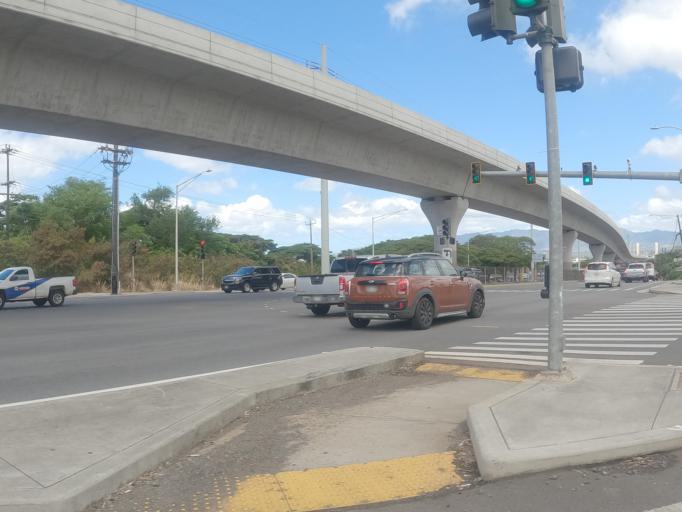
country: US
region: Hawaii
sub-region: Honolulu County
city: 'Aiea
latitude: 21.3795
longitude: -157.9370
